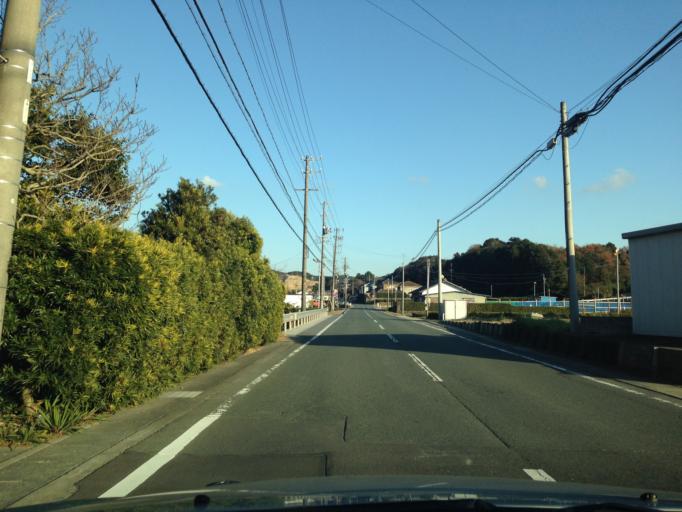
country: JP
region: Shizuoka
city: Fukuroi
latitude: 34.7360
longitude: 137.9474
